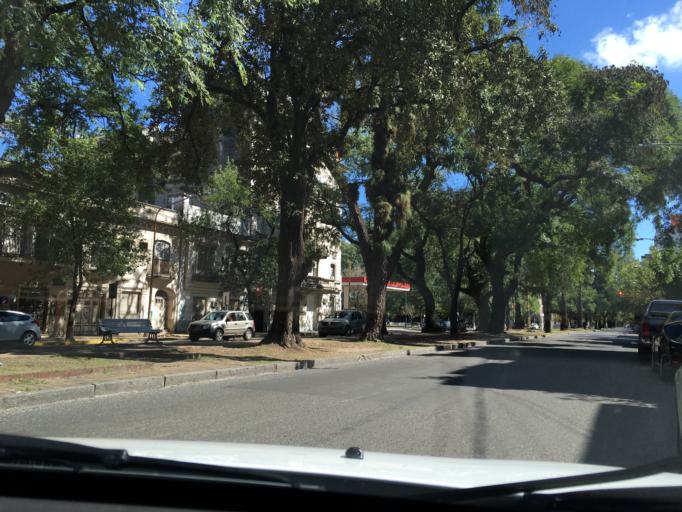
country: AR
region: Santa Fe
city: Santa Fe de la Vera Cruz
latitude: -31.6380
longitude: -60.6913
